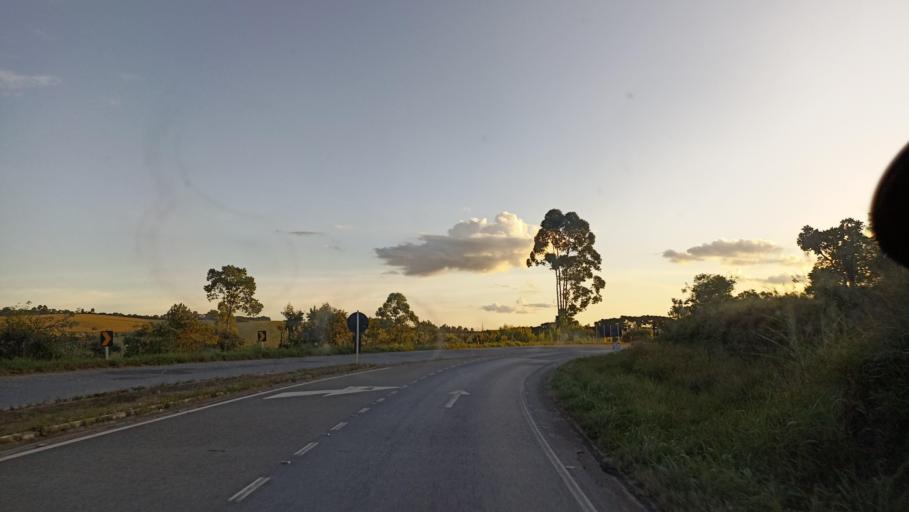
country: BR
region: Minas Gerais
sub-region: Sao Joao Del Rei
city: Sao Joao del Rei
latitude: -21.2297
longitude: -44.3768
